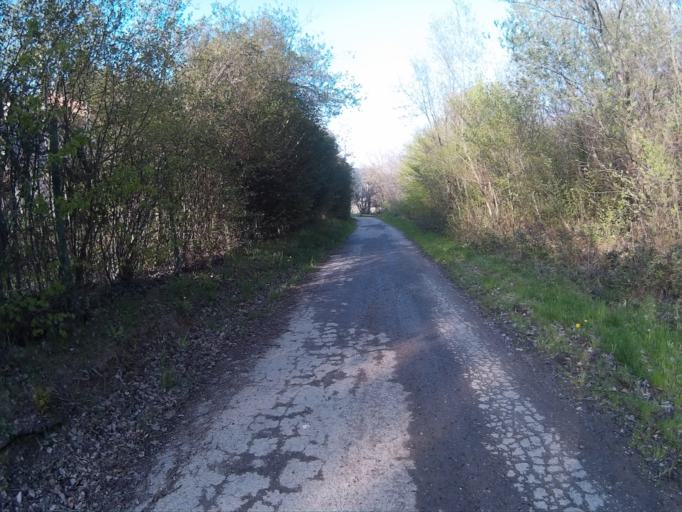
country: AT
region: Burgenland
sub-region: Politischer Bezirk Oberwart
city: Rechnitz
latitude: 47.3418
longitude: 16.4910
